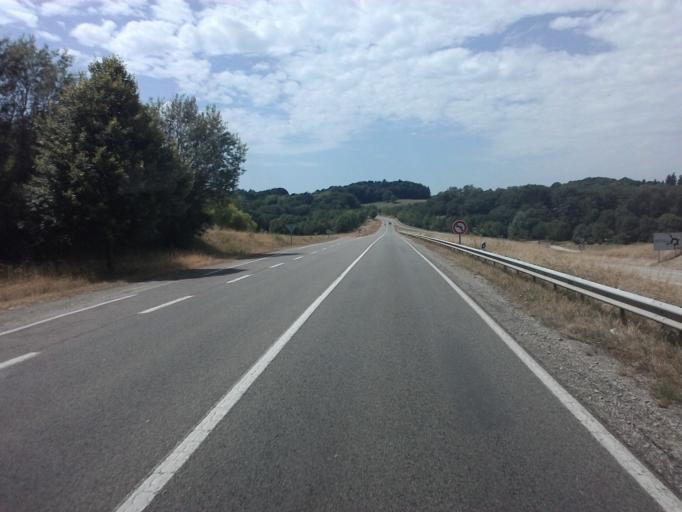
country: FR
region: Bourgogne
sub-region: Departement de Saone-et-Loire
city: Cuiseaux
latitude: 46.4836
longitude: 5.3689
